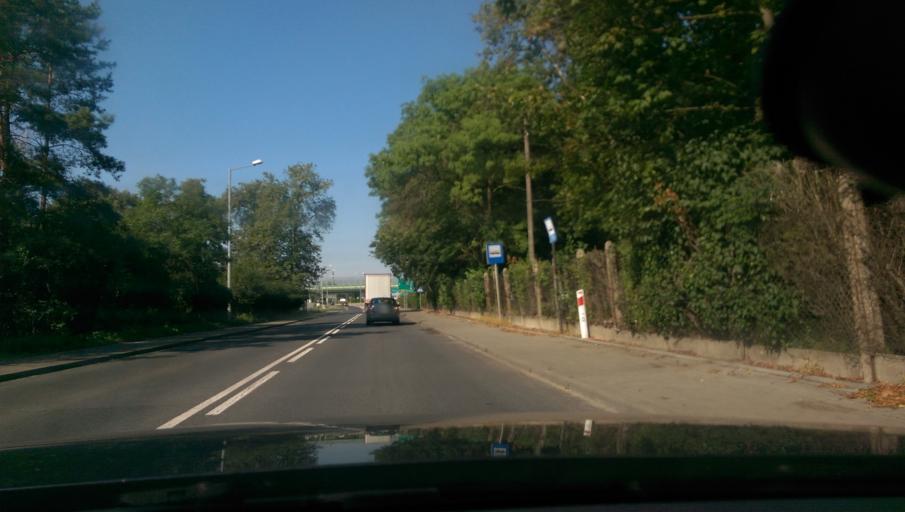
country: PL
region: Masovian Voivodeship
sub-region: Powiat plonski
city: Plonsk
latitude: 52.6326
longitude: 20.3864
